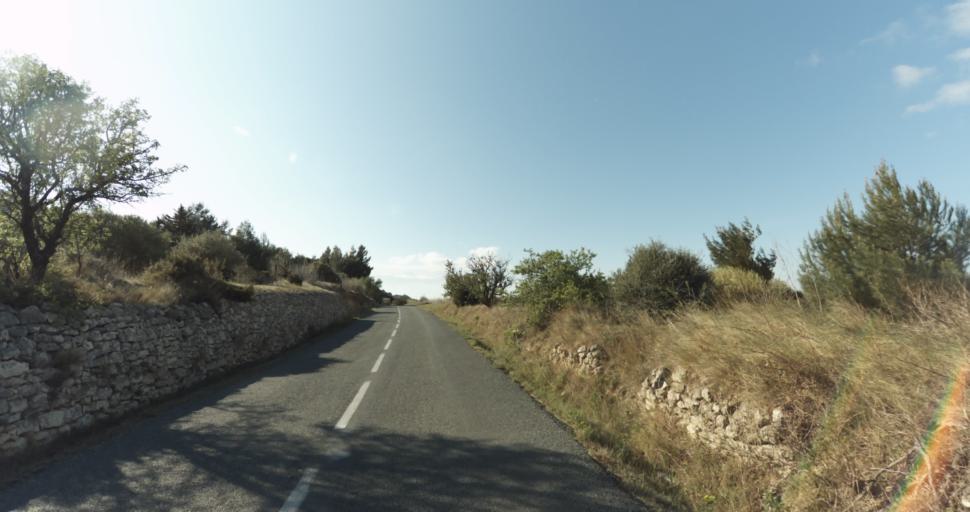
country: FR
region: Languedoc-Roussillon
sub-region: Departement de l'Aude
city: Leucate
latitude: 42.9229
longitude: 3.0149
